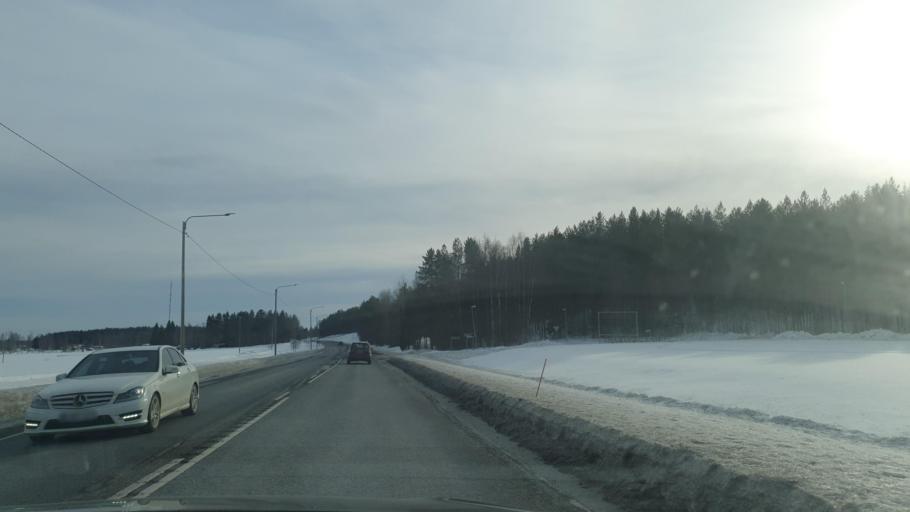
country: FI
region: Northern Ostrobothnia
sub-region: Oulu
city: Muhos
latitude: 64.8429
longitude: 25.9027
